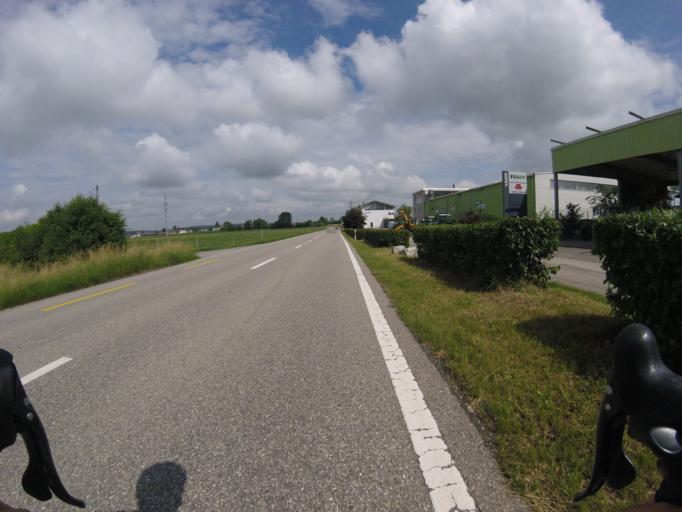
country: CH
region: Bern
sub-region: Emmental District
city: Hindelbank
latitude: 47.0352
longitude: 7.5483
